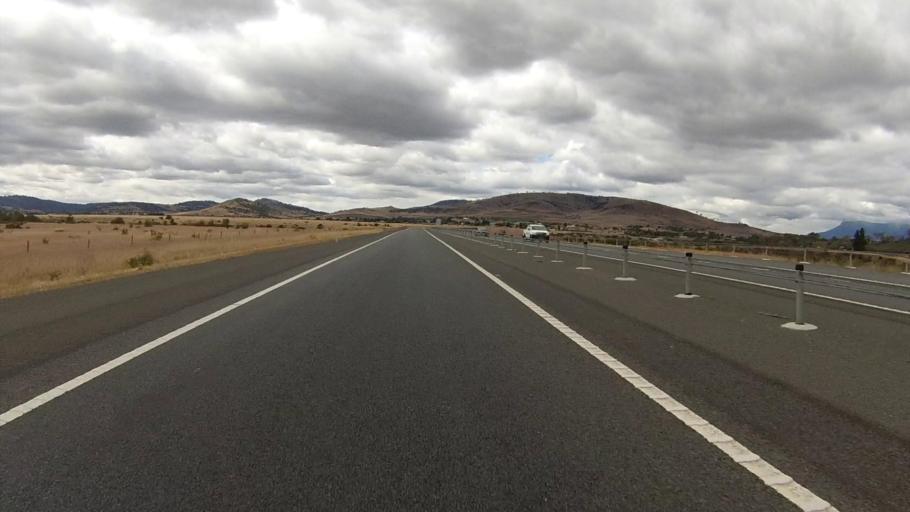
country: AU
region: Tasmania
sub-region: Brighton
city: Bridgewater
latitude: -42.6796
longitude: 147.2735
